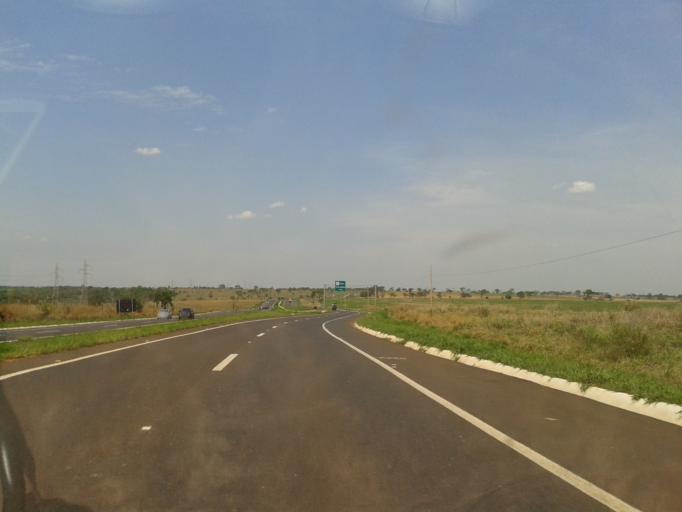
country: BR
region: Minas Gerais
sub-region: Monte Alegre De Minas
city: Monte Alegre de Minas
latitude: -18.8497
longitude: -48.8280
